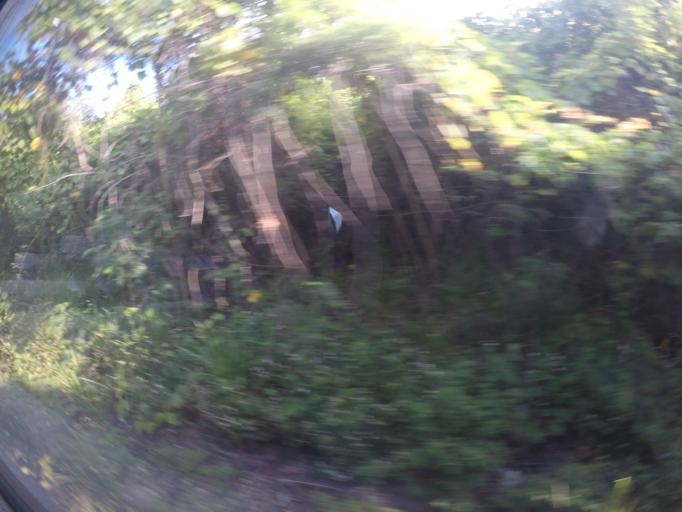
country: VN
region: Khanh Hoa
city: Van Gia
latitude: 12.8367
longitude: 109.3740
